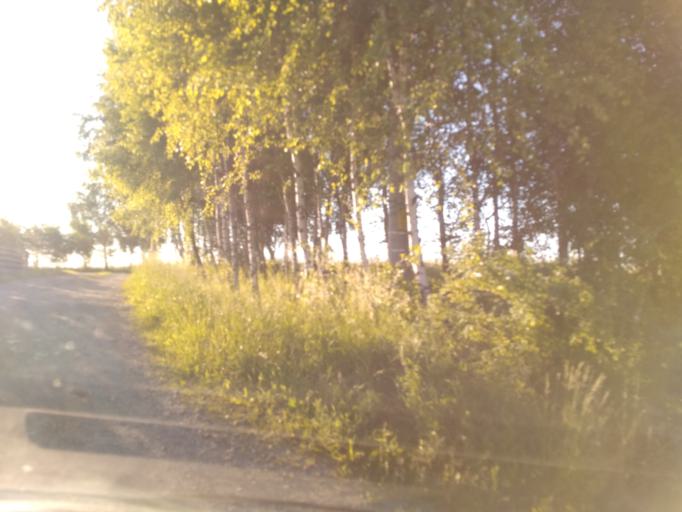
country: PL
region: Subcarpathian Voivodeship
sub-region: Powiat rzeszowski
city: Lubenia
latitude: 49.9202
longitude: 21.9139
